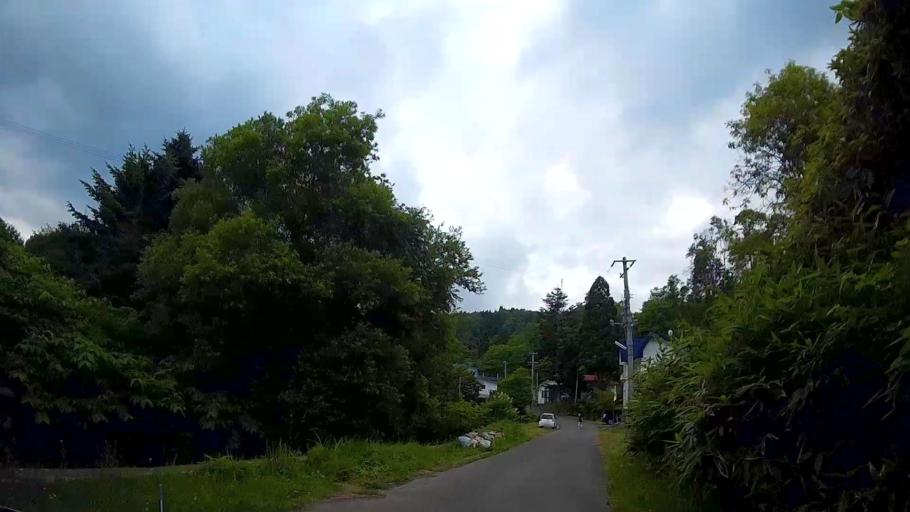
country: JP
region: Hokkaido
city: Nanae
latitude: 42.1184
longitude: 140.5375
